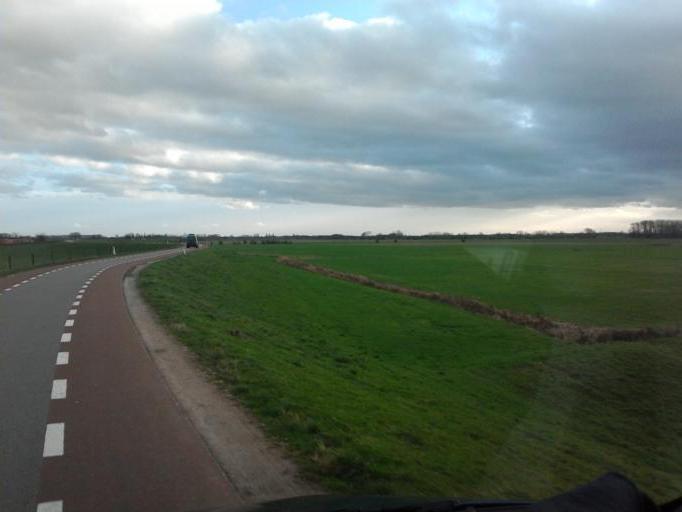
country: NL
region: Gelderland
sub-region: Gemeente Culemborg
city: Culemborg
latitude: 51.9787
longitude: 5.2590
